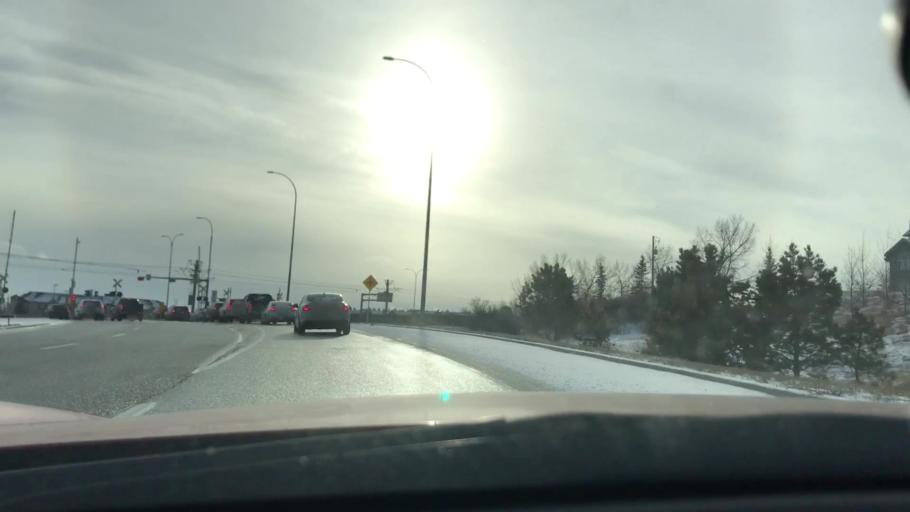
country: CA
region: Alberta
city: Calgary
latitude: 51.0404
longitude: -114.1663
